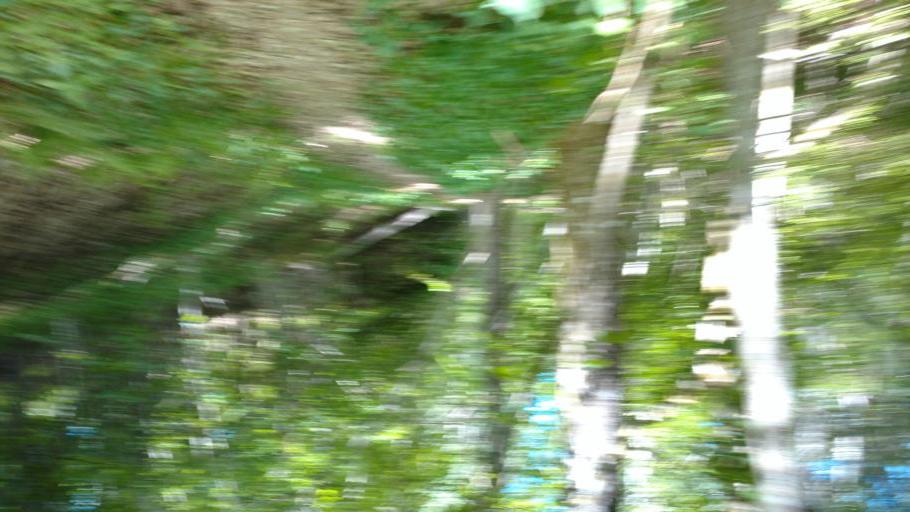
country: FI
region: Uusimaa
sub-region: Raaseporin
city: Pohja
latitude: 60.1094
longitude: 23.5489
